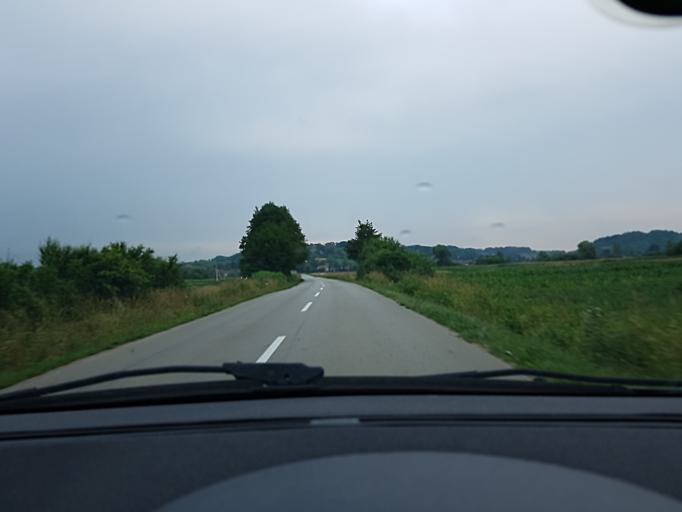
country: HR
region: Zagrebacka
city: Pojatno
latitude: 45.9458
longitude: 15.8124
